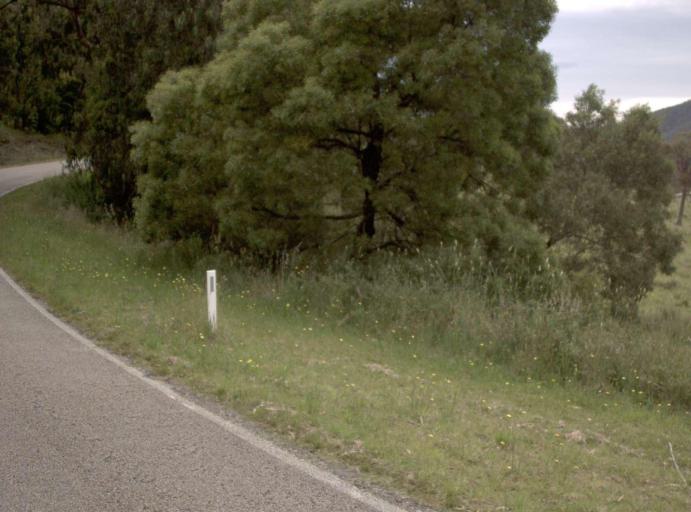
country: AU
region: Victoria
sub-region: East Gippsland
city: Bairnsdale
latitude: -37.5759
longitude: 147.1824
